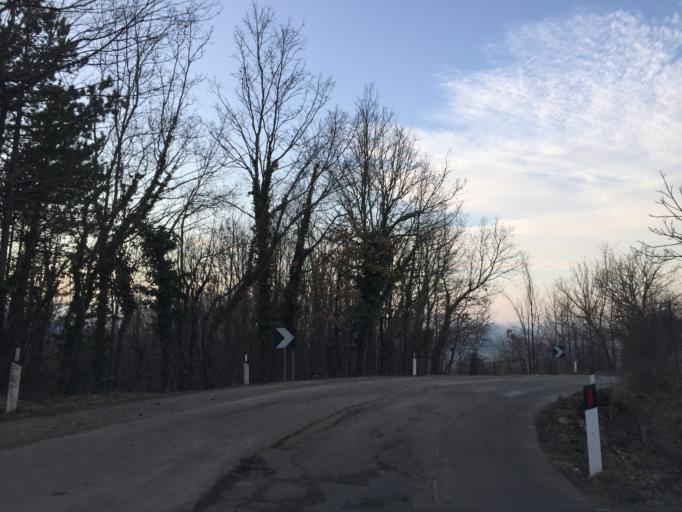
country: IT
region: Molise
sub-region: Provincia di Campobasso
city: Guardiaregia
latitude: 41.4432
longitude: 14.5481
